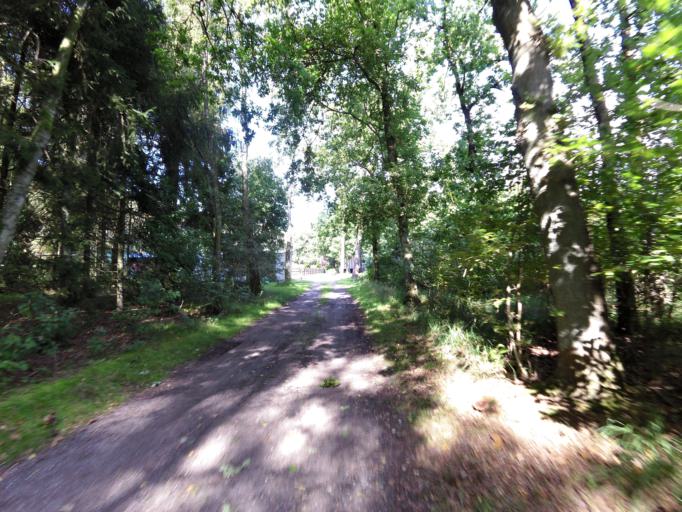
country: NL
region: North Brabant
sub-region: Gemeente Woensdrecht
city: Woensdrecht
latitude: 51.4457
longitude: 4.3647
